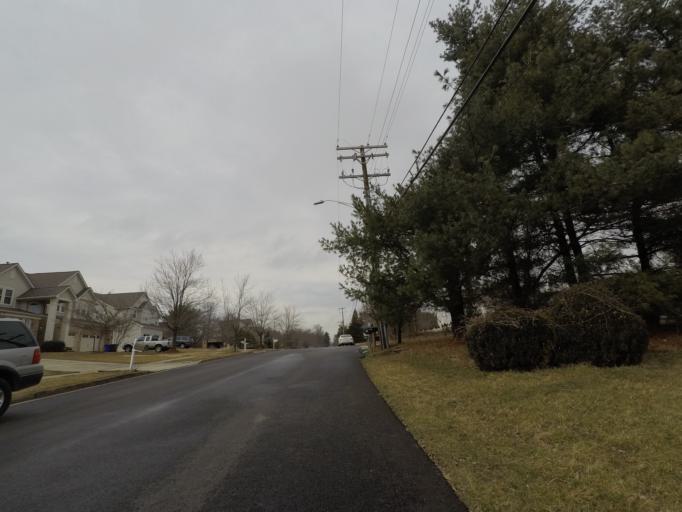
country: US
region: Maryland
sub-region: Howard County
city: Ilchester
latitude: 39.2233
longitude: -76.7783
